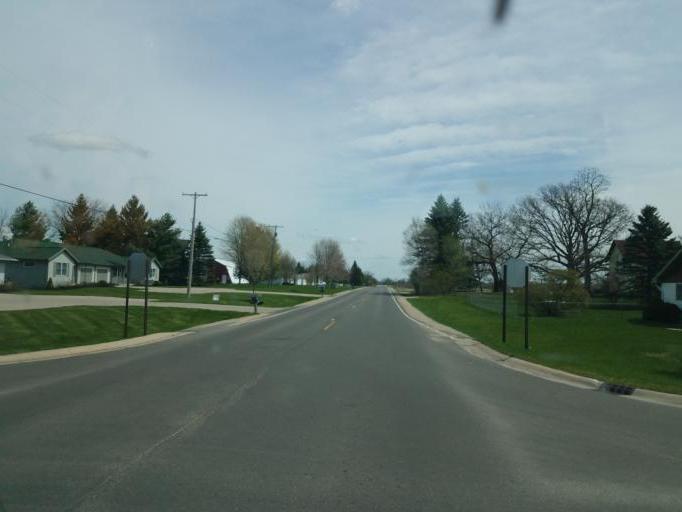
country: US
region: Michigan
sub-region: Isabella County
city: Mount Pleasant
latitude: 43.6260
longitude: -84.8082
